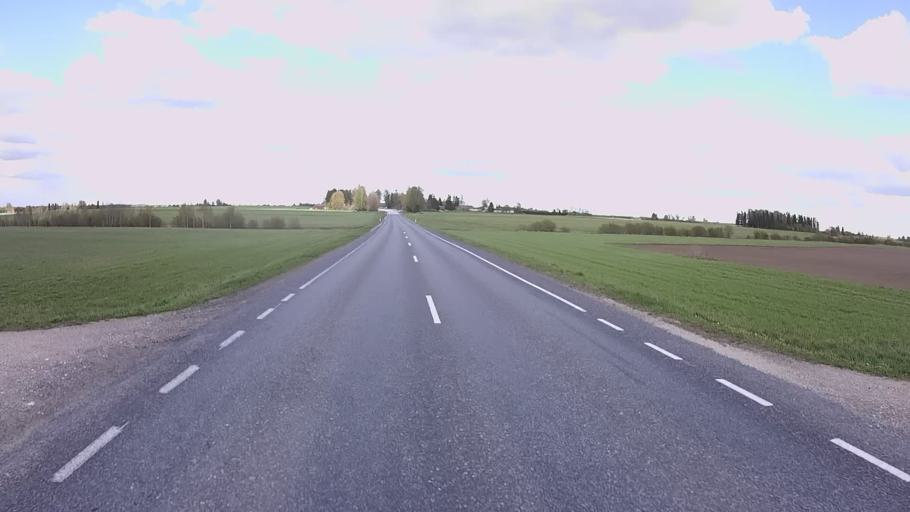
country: EE
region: Jogevamaa
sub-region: Jogeva linn
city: Jogeva
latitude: 58.8044
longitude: 26.5135
